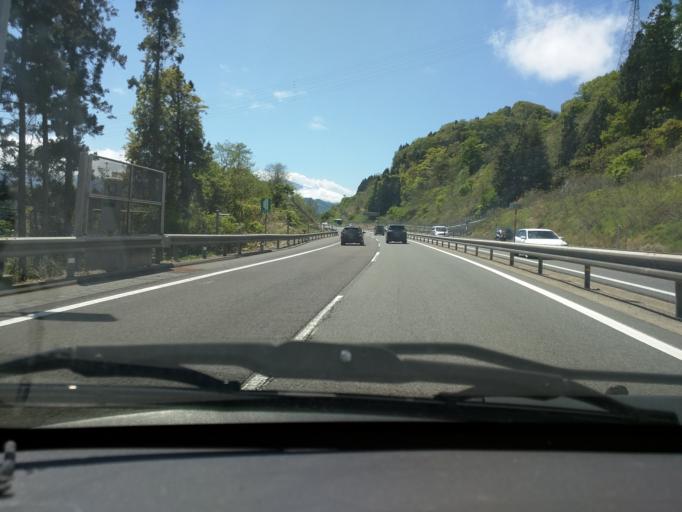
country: JP
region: Nagano
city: Nakano
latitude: 36.7806
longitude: 138.3172
